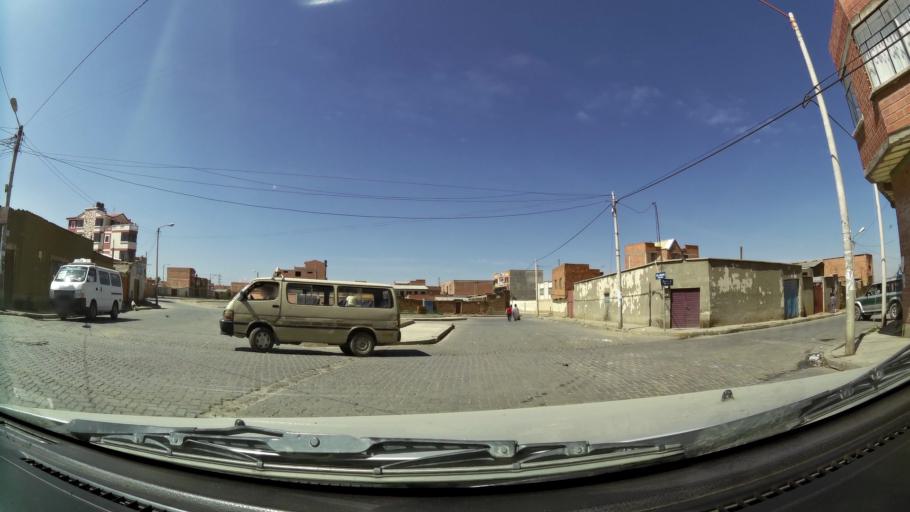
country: BO
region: La Paz
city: La Paz
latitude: -16.5362
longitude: -68.1603
